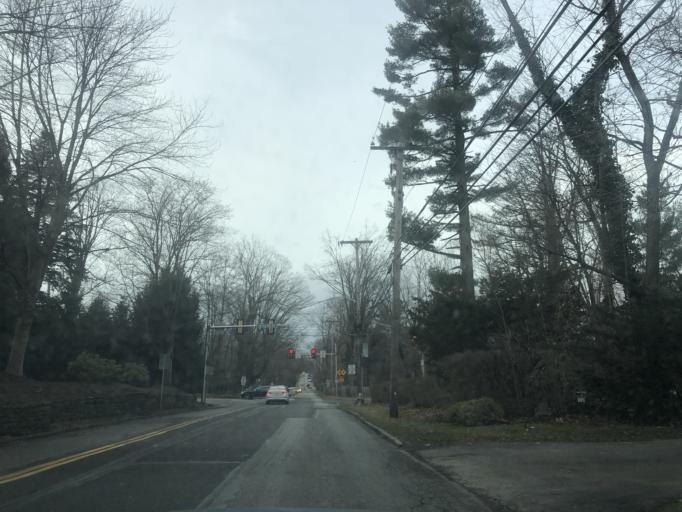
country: US
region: Pennsylvania
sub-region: Delaware County
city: Radnor
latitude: 40.0413
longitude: -75.3323
